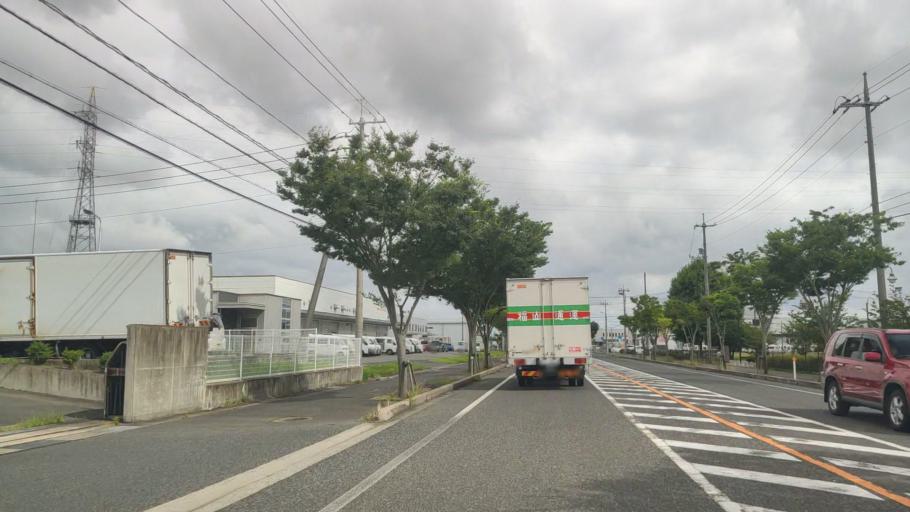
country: JP
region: Tottori
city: Yonago
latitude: 35.4285
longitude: 133.3946
